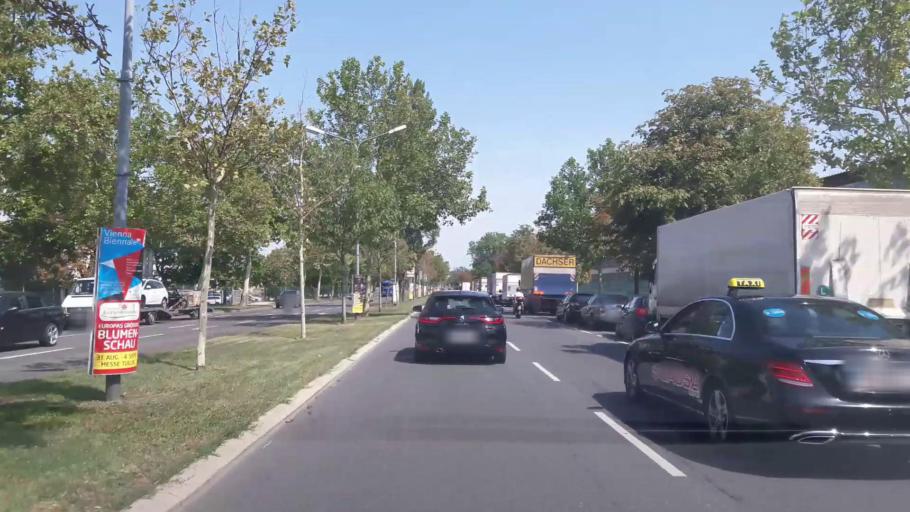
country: AT
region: Lower Austria
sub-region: Politischer Bezirk Modling
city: Vosendorf
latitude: 48.1365
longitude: 16.3573
